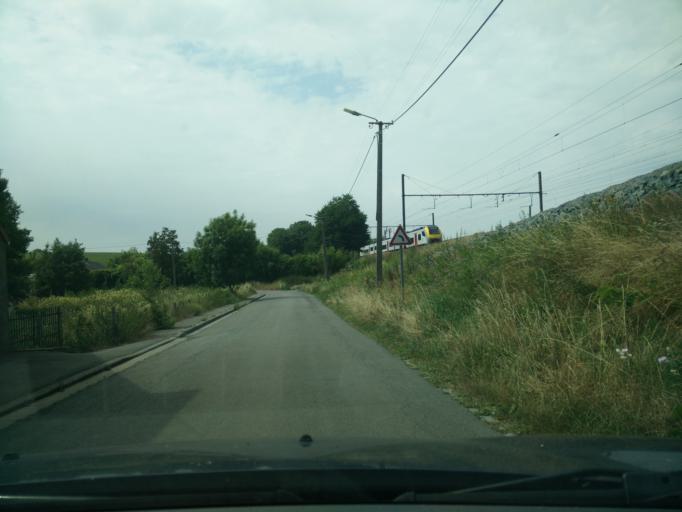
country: BE
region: Wallonia
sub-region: Province du Hainaut
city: Braine-le-Comte
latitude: 50.6482
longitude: 4.1739
